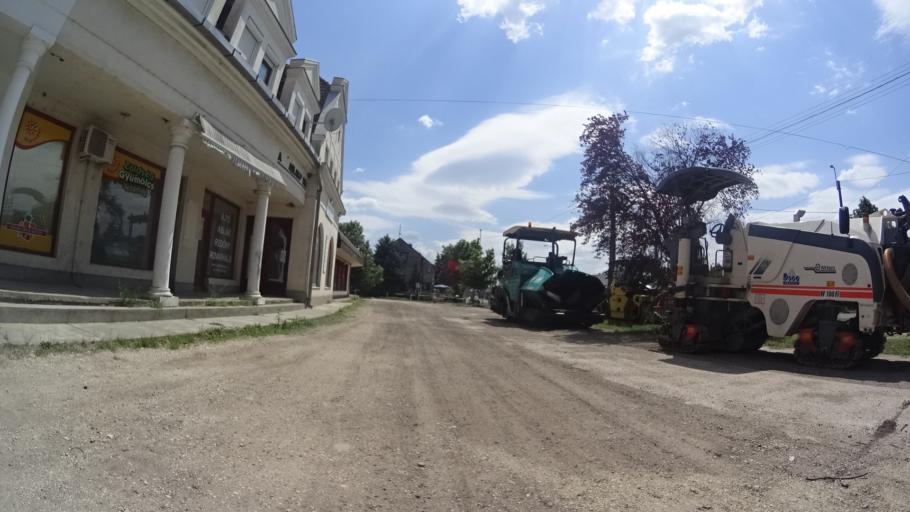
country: HU
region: Bacs-Kiskun
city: Tiszakecske
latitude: 46.9397
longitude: 20.0978
